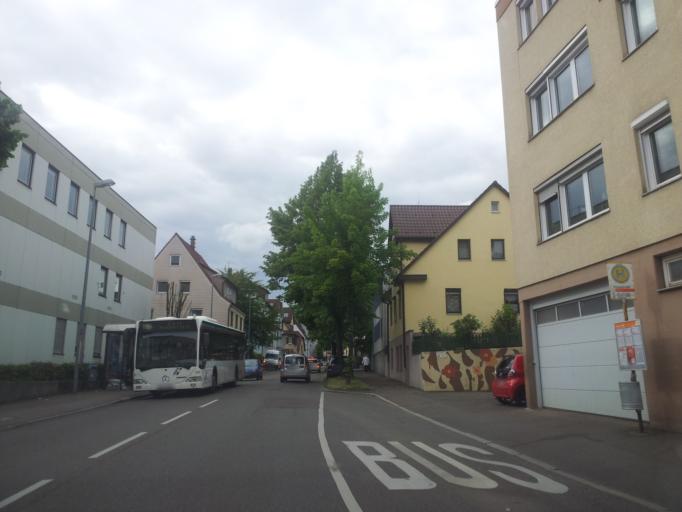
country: DE
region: Baden-Wuerttemberg
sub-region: Regierungsbezirk Stuttgart
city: Esslingen
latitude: 48.7329
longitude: 9.3319
